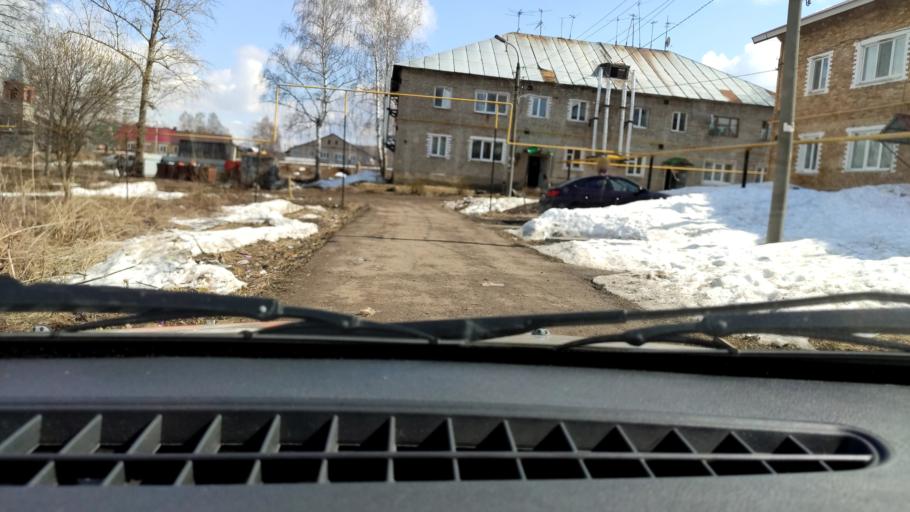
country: RU
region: Bashkortostan
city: Kudeyevskiy
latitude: 54.8684
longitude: 56.7452
